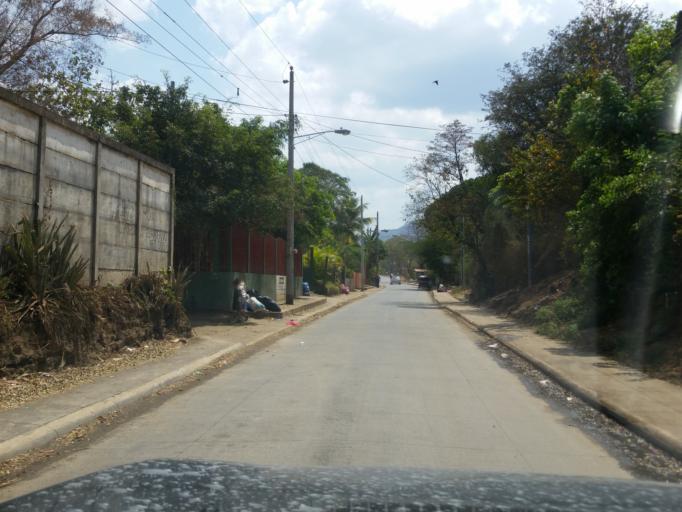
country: NI
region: Masaya
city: Ticuantepe
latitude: 12.0706
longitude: -86.1987
